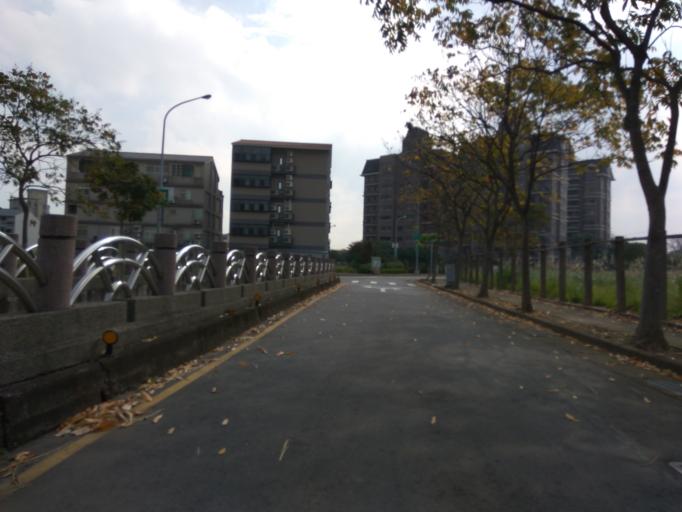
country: TW
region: Taiwan
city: Taoyuan City
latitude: 25.0055
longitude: 121.2179
